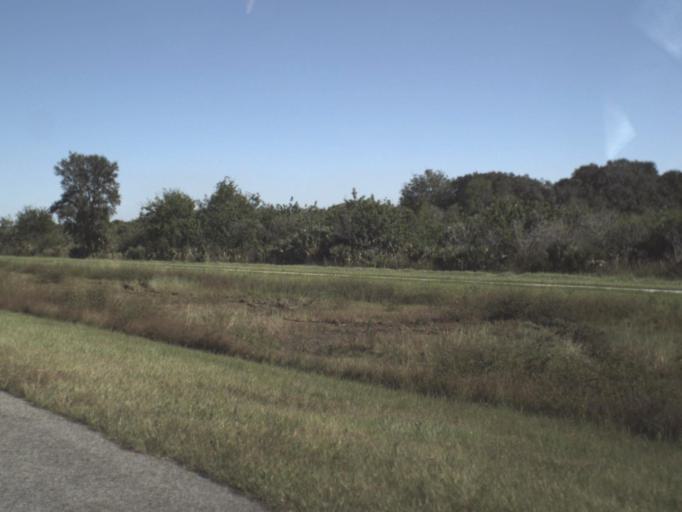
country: US
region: Florida
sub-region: Hendry County
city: Port LaBelle
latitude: 26.7622
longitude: -81.4068
